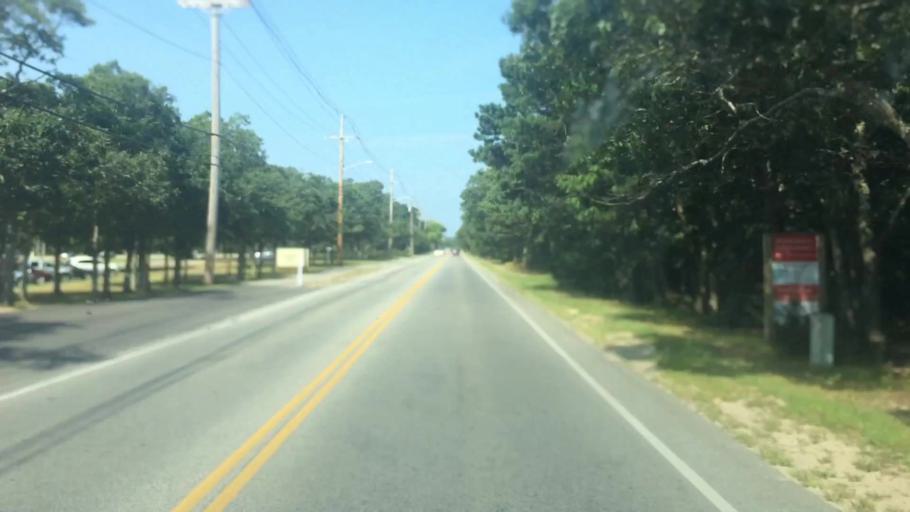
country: US
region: Massachusetts
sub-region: Dukes County
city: Vineyard Haven
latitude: 41.4189
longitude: -70.5946
